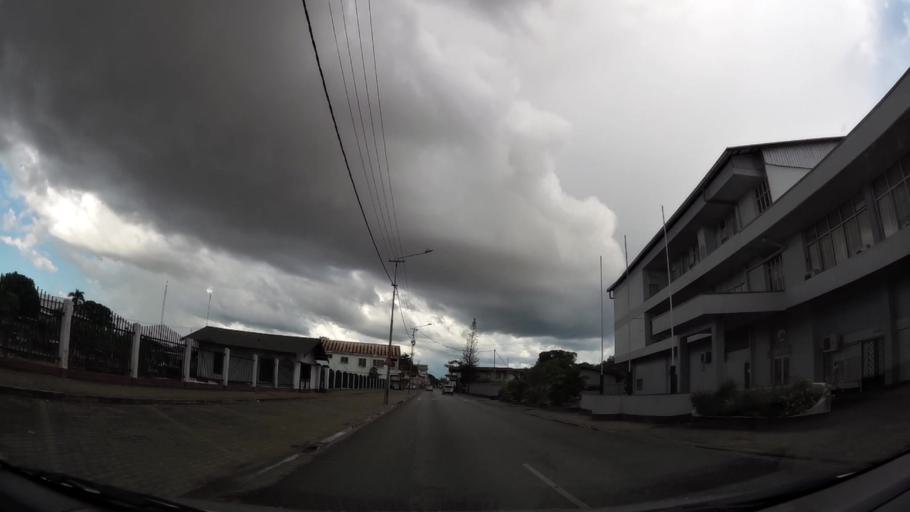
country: SR
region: Paramaribo
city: Paramaribo
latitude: 5.8348
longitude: -55.1676
